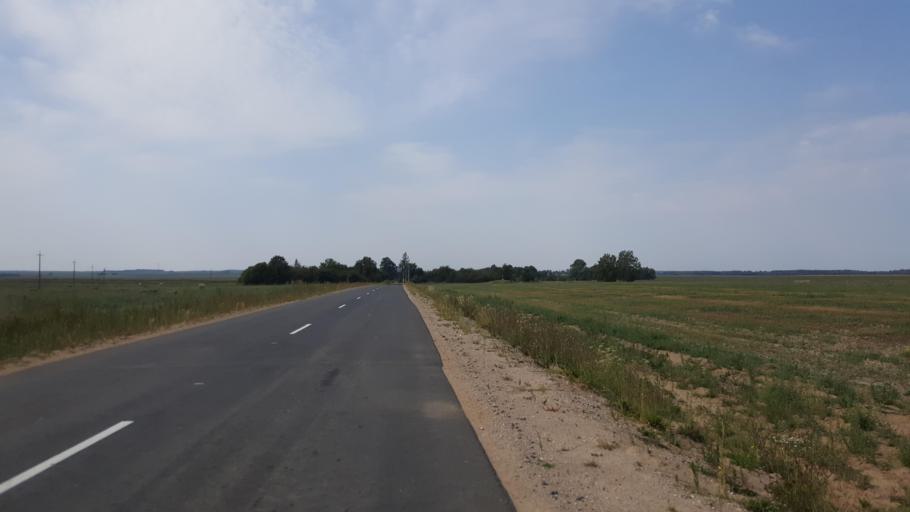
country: BY
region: Brest
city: Kamyanyets
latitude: 52.4539
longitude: 23.6608
